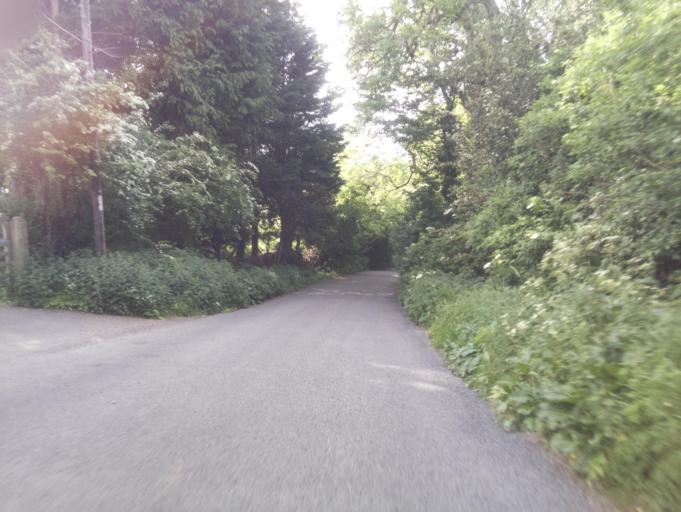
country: GB
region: England
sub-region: Gloucestershire
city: Chipping Campden
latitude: 52.0577
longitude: -1.8085
